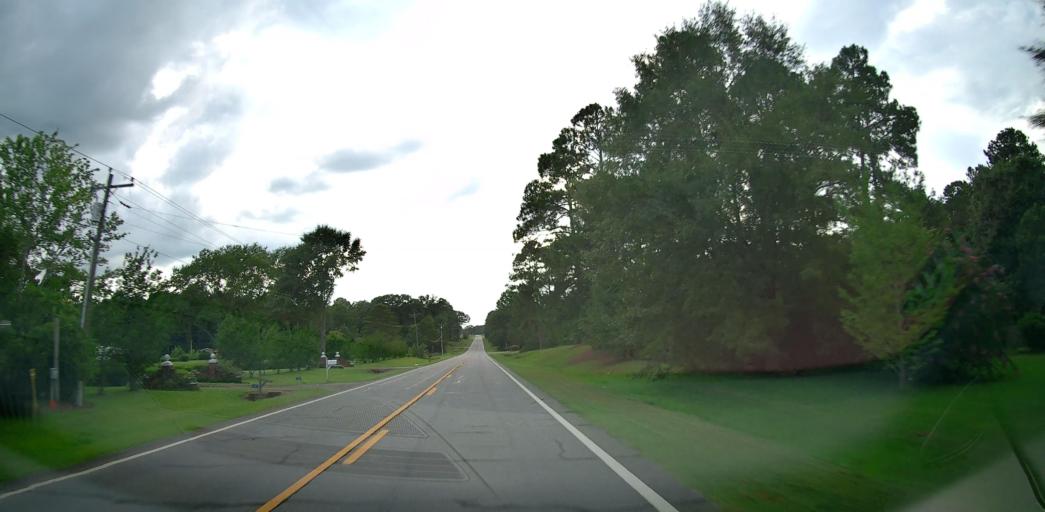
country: US
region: Georgia
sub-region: Pulaski County
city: Hawkinsville
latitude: 32.2893
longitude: -83.4985
